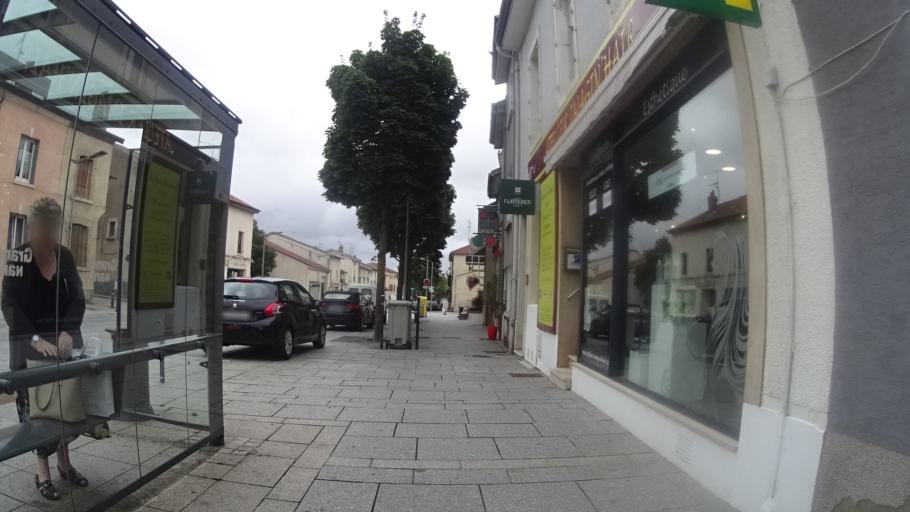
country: FR
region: Lorraine
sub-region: Departement de Meurthe-et-Moselle
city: Laneuveville-devant-Nancy
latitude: 48.6566
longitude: 6.2312
